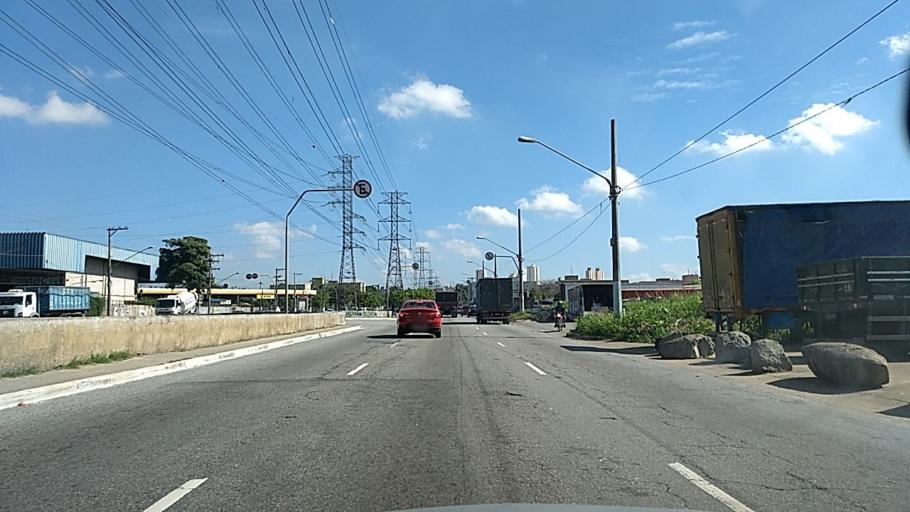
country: BR
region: Sao Paulo
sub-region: Guarulhos
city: Guarulhos
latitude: -23.4890
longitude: -46.5633
